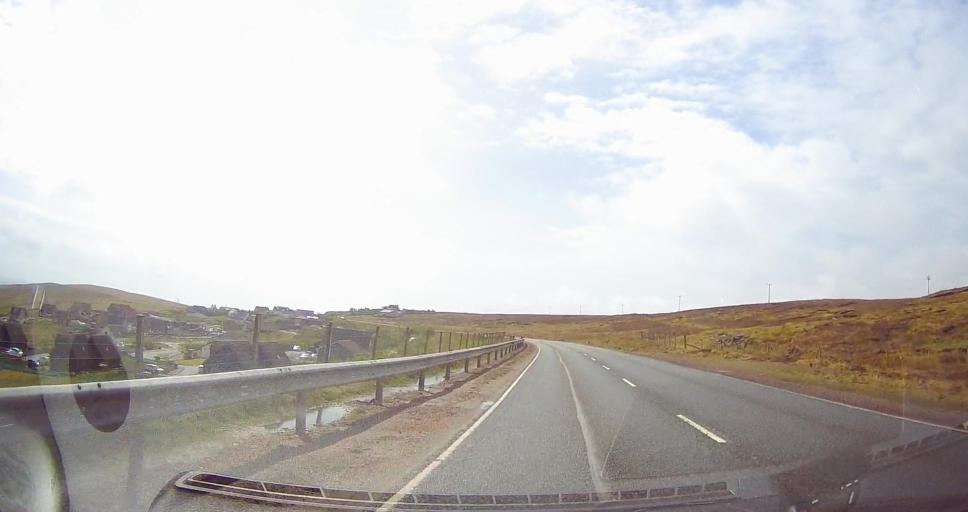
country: GB
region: Scotland
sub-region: Shetland Islands
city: Lerwick
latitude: 60.1269
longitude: -1.2165
